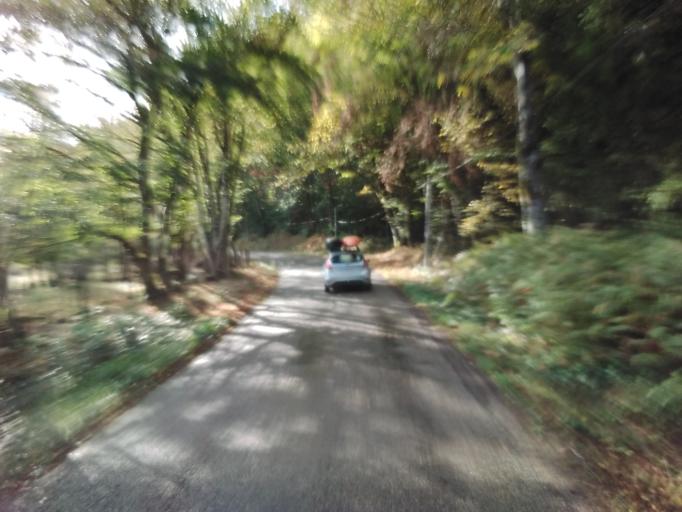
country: FR
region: Bourgogne
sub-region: Departement de la Nievre
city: Lormes
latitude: 47.2918
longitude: 3.8486
